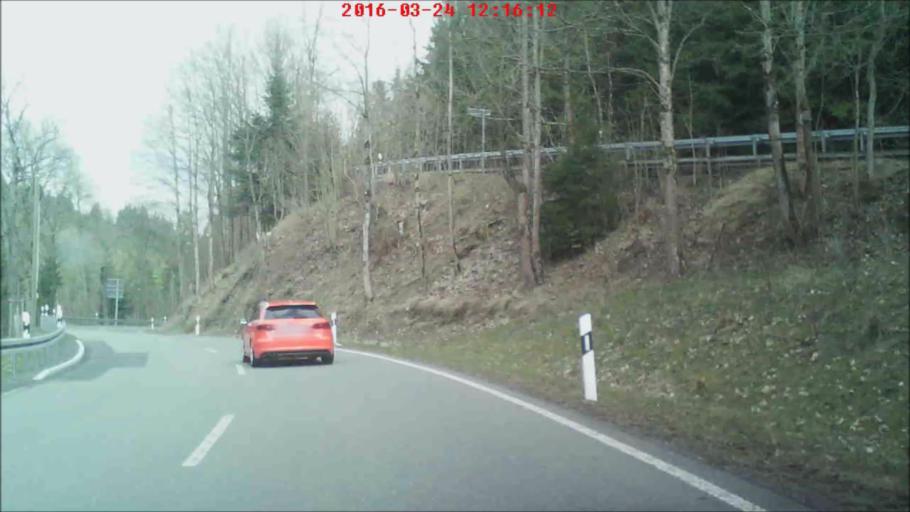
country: DE
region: Thuringia
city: Meuselbach
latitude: 50.5708
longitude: 11.0717
